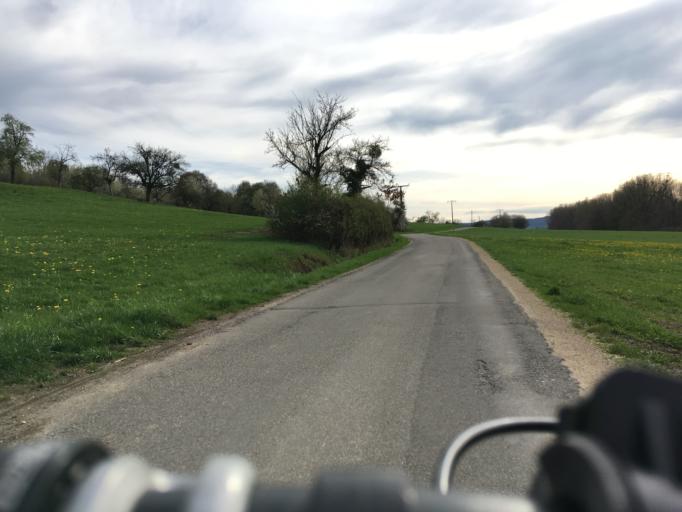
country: DE
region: Baden-Wuerttemberg
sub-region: Freiburg Region
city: Neuhausen
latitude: 47.8027
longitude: 8.7375
